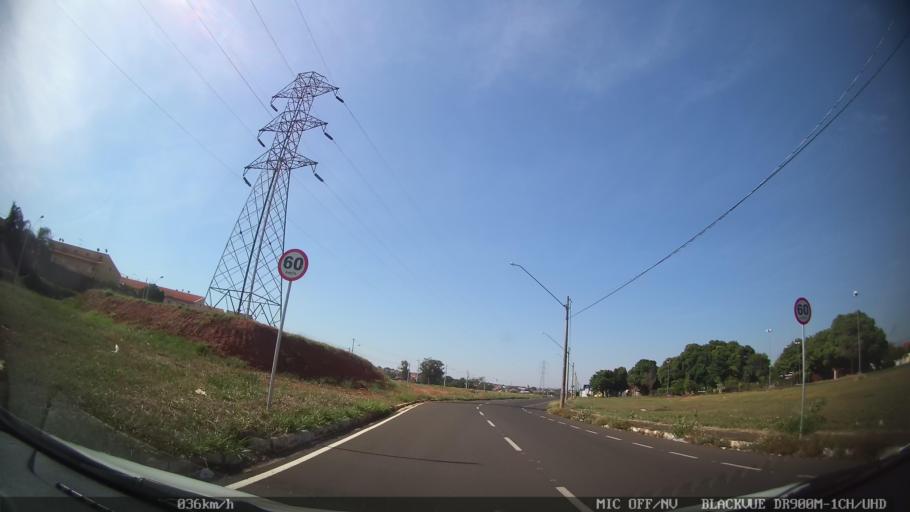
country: BR
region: Sao Paulo
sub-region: Sao Jose Do Rio Preto
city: Sao Jose do Rio Preto
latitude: -20.7902
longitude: -49.4186
